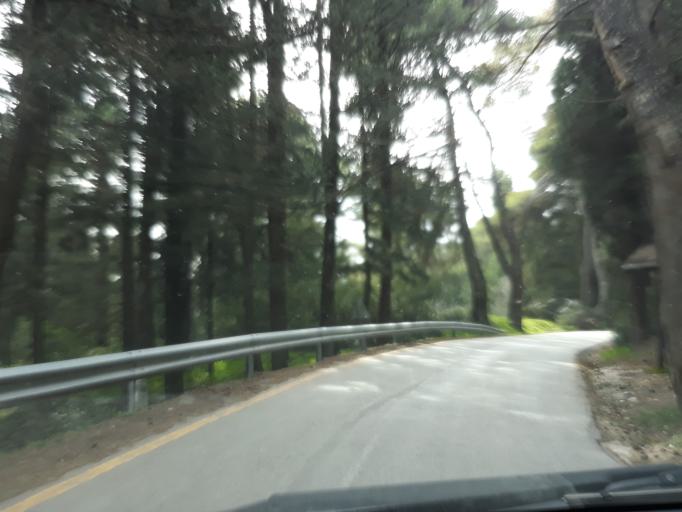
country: GR
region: Attica
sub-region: Nomarchia Anatolikis Attikis
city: Varybobi
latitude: 38.1608
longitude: 23.7908
